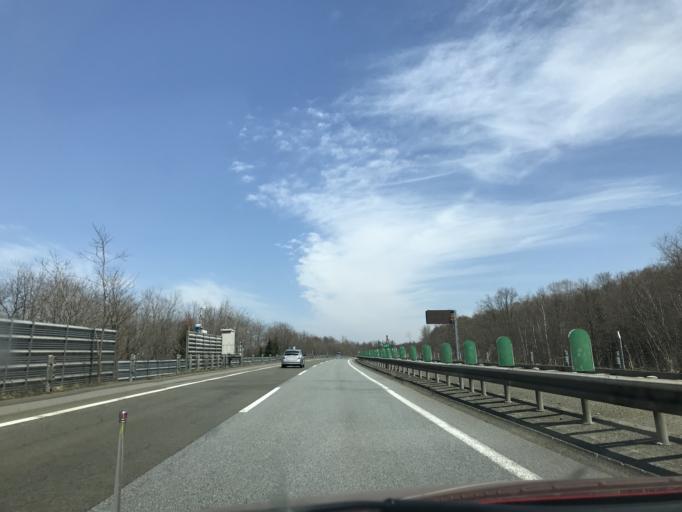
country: JP
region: Hokkaido
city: Bibai
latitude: 43.2918
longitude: 141.8652
